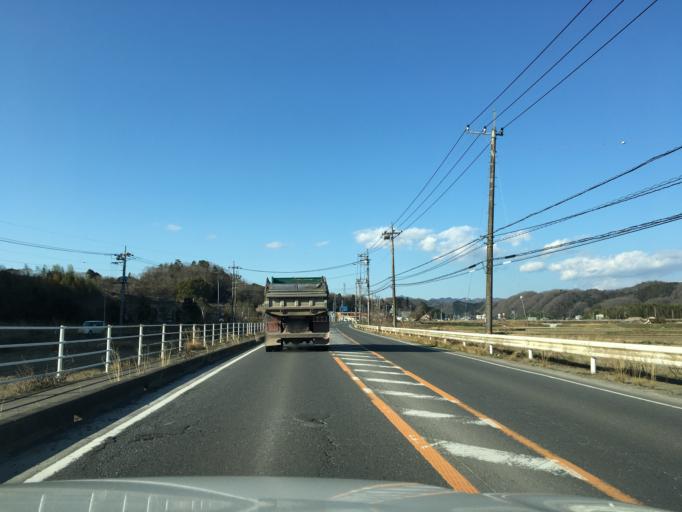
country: JP
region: Ibaraki
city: Omiya
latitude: 36.6091
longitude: 140.3982
